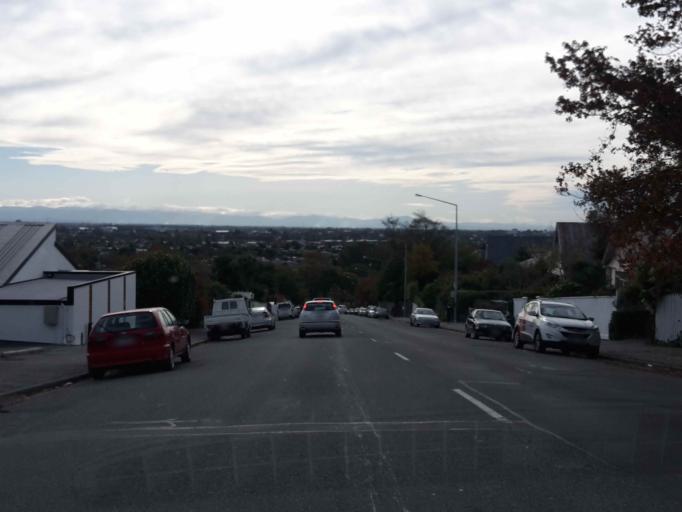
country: NZ
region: Canterbury
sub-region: Christchurch City
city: Christchurch
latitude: -43.5725
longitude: 172.6245
